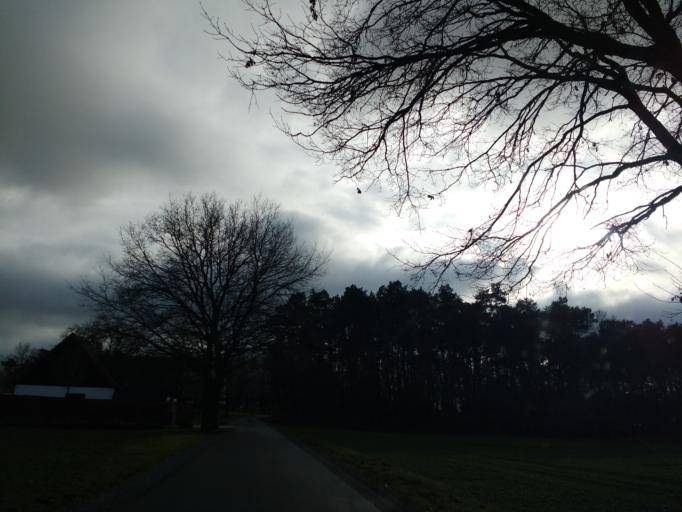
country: DE
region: North Rhine-Westphalia
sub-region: Regierungsbezirk Detmold
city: Hovelhof
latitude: 51.8379
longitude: 8.6762
